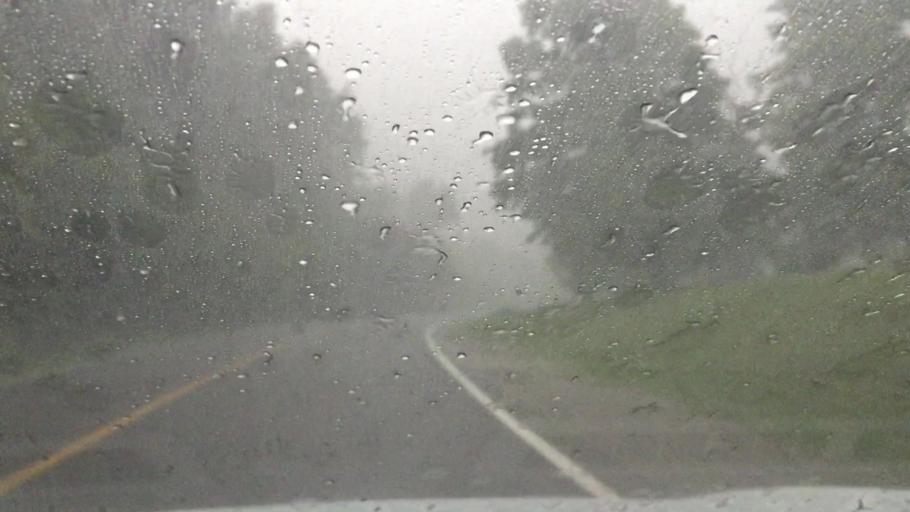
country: CA
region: Ontario
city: Markham
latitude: 43.8499
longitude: -79.2012
